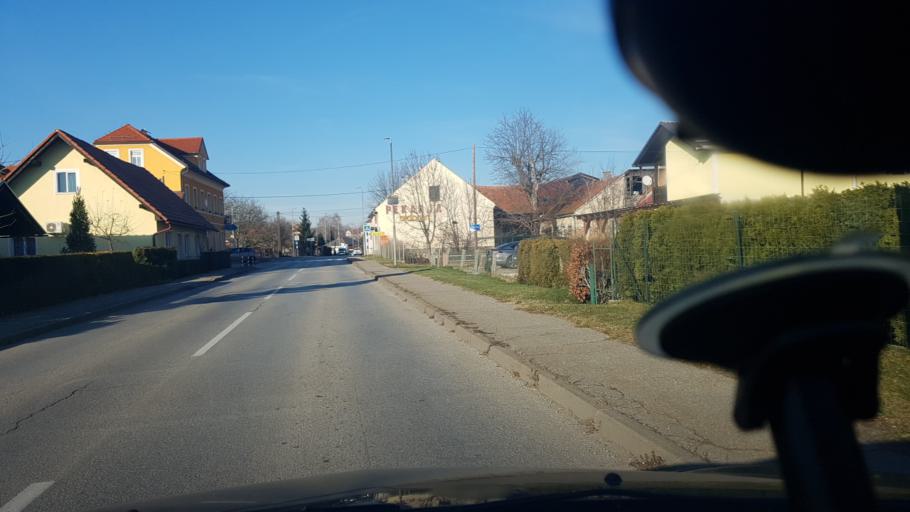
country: SI
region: Ptuj
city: Ptuj
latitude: 46.4133
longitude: 15.8647
